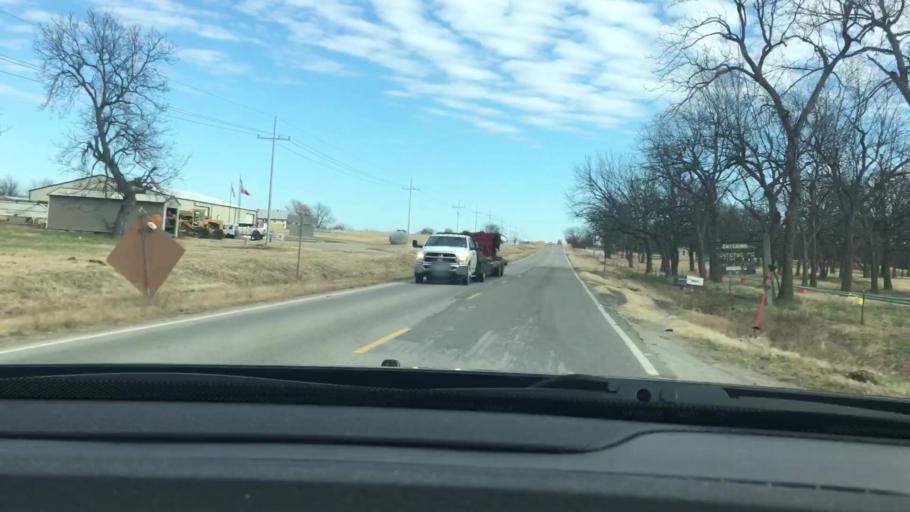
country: US
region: Oklahoma
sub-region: Garvin County
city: Stratford
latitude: 34.7966
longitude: -96.9322
